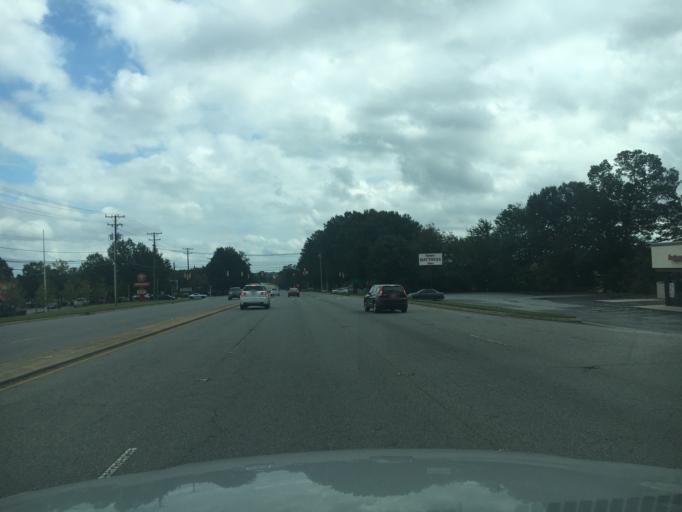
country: US
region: North Carolina
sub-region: Catawba County
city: Hickory
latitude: 35.7014
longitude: -81.2908
